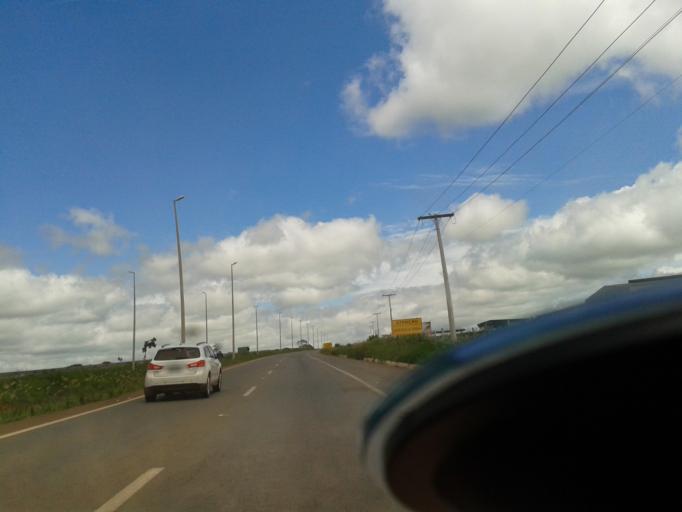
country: BR
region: Goias
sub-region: Goianira
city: Goianira
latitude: -16.4631
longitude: -49.4418
